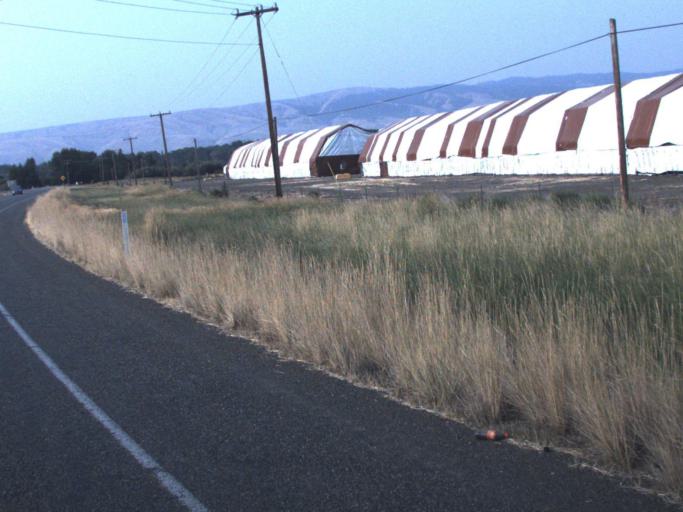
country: US
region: Washington
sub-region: Kittitas County
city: Ellensburg
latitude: 47.0178
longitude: -120.5926
